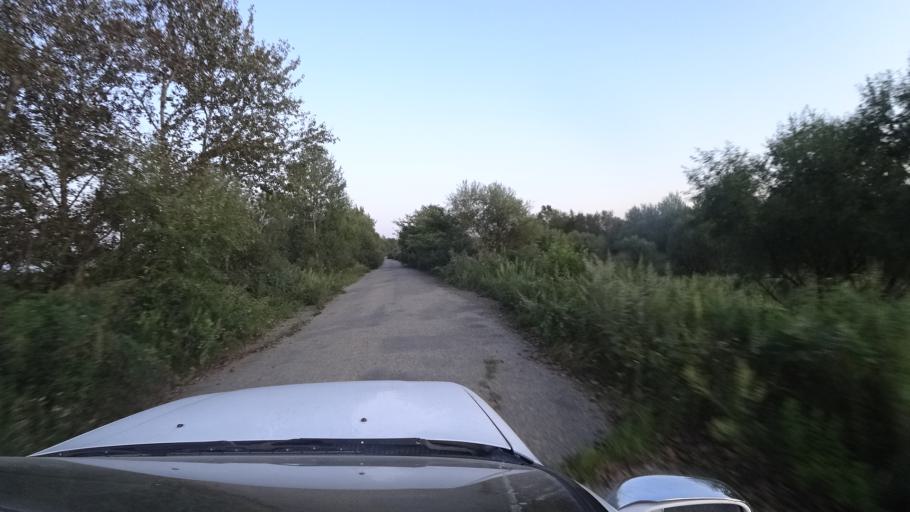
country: RU
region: Primorskiy
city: Dal'nerechensk
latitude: 45.9479
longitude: 133.7627
